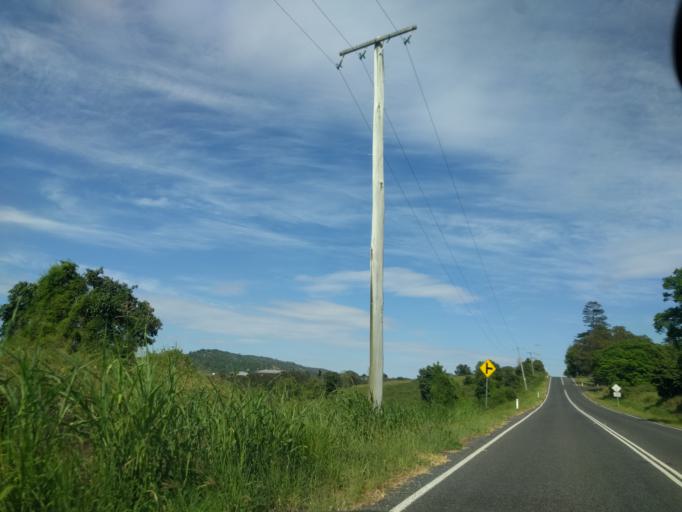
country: AU
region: Queensland
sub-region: Ipswich
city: Thagoona
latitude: -27.5949
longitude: 152.5670
